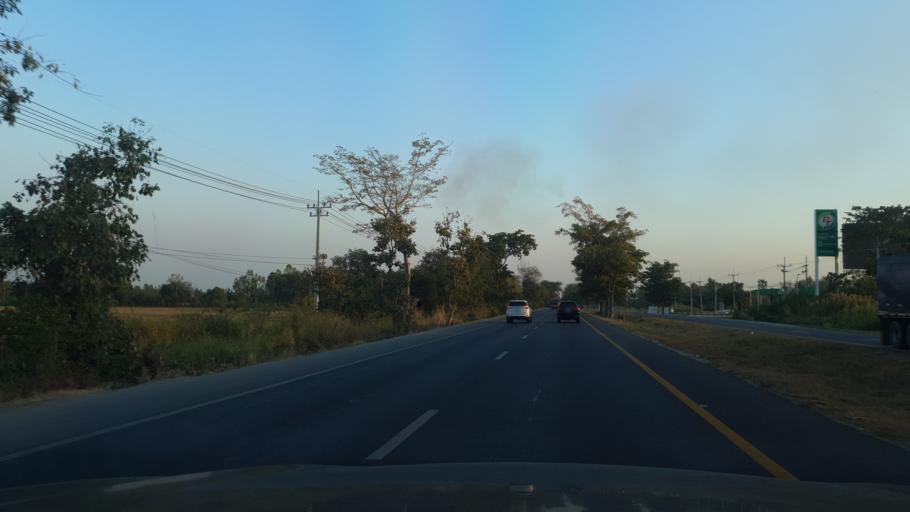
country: TH
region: Nakhon Sawan
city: Banphot Phisai
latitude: 15.8751
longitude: 99.9092
